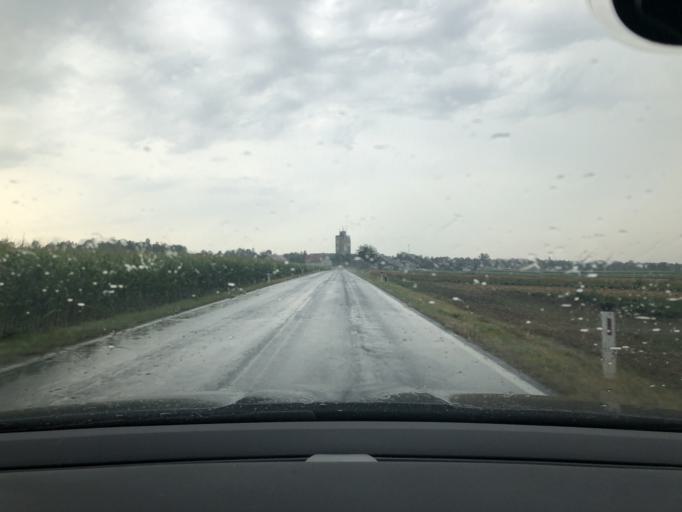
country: AT
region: Lower Austria
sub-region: Politischer Bezirk Ganserndorf
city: Marchegg
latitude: 48.3056
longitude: 16.8423
